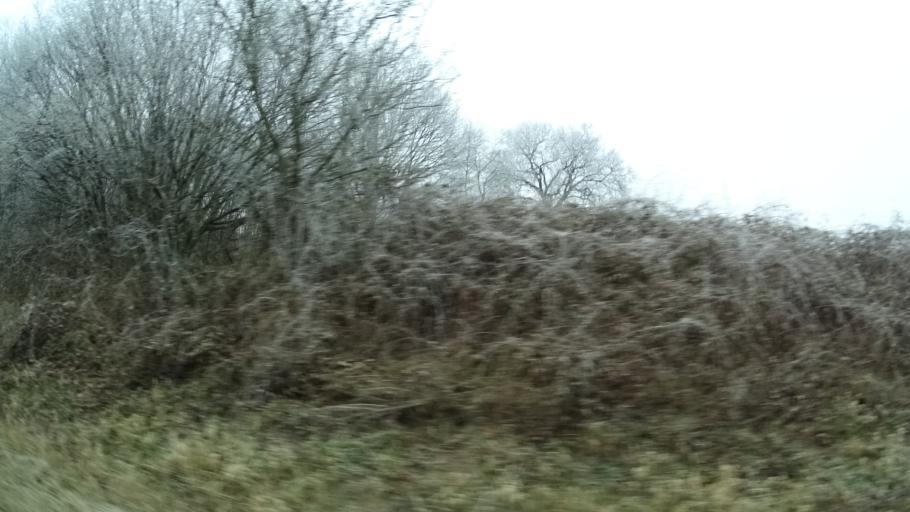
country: DE
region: Bavaria
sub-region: Regierungsbezirk Unterfranken
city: Schollkrippen
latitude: 50.0955
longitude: 9.2555
